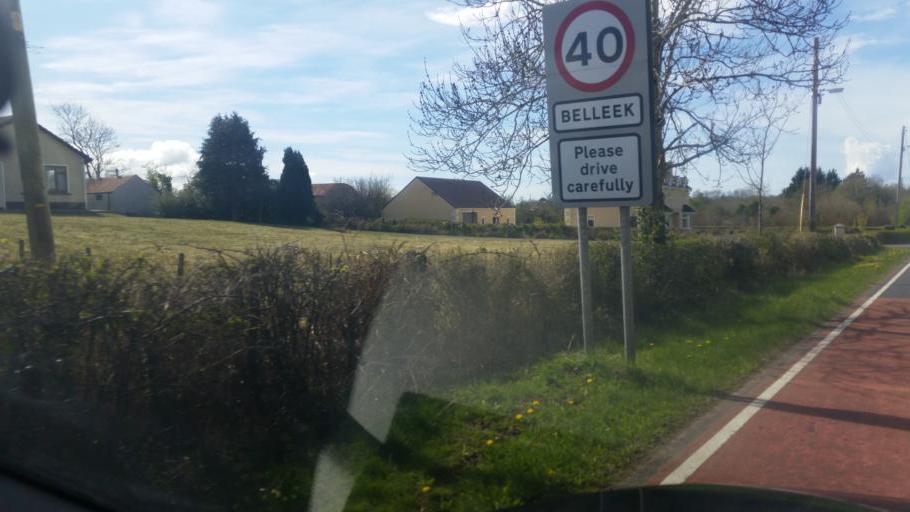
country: IE
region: Ulster
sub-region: County Donegal
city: Ballyshannon
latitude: 54.4742
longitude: -8.0887
